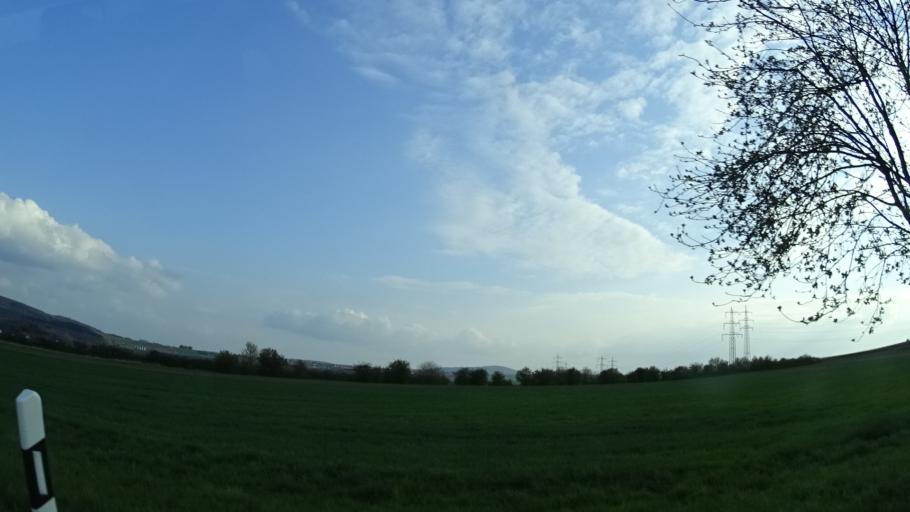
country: DE
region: Rheinland-Pfalz
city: Rudesheim
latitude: 49.8509
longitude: 7.8001
